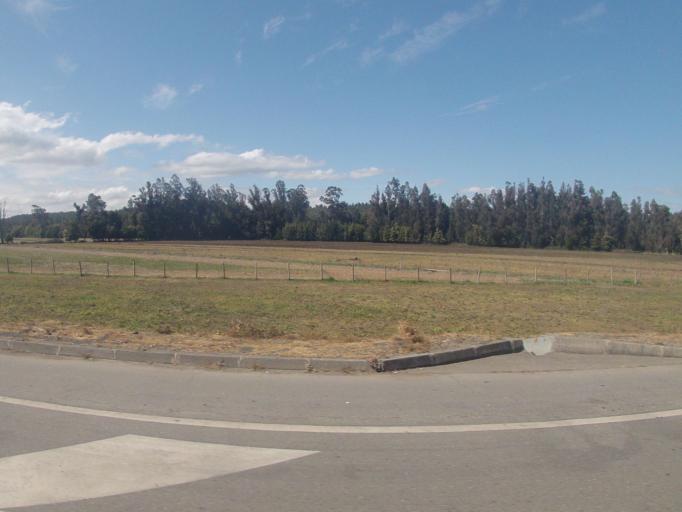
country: CL
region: Biobio
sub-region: Provincia de Biobio
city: Los Angeles
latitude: -37.4381
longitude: -72.3959
